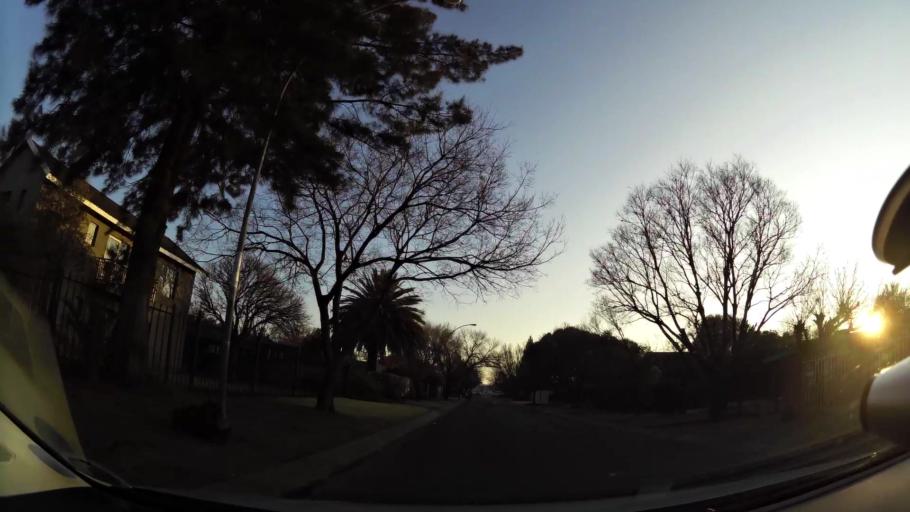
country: ZA
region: Orange Free State
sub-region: Mangaung Metropolitan Municipality
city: Bloemfontein
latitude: -29.1038
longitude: 26.1585
